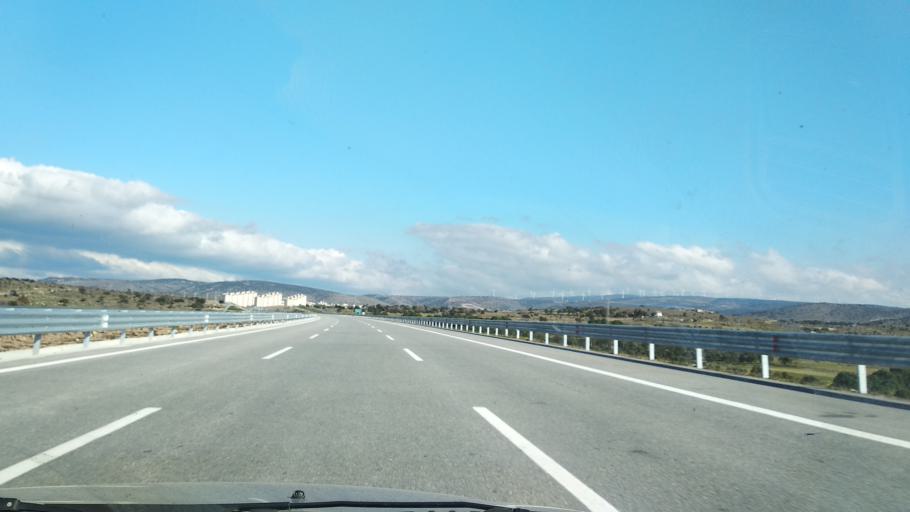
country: TR
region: Izmir
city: Yenisakran
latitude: 38.8660
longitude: 27.0808
